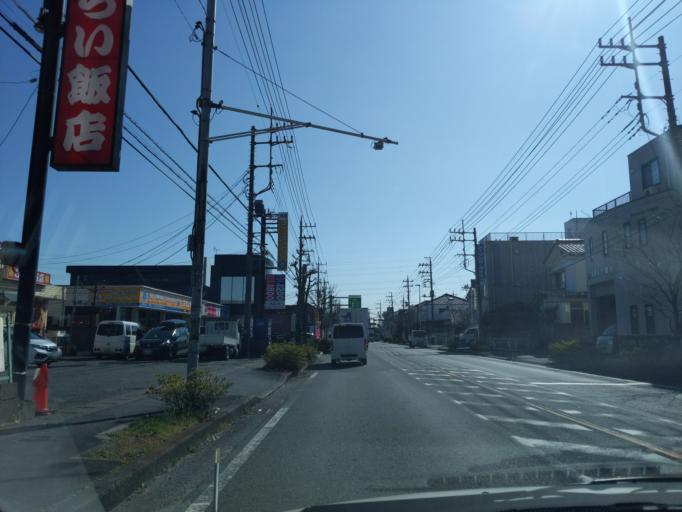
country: JP
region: Saitama
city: Yashio-shi
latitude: 35.8217
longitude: 139.8255
